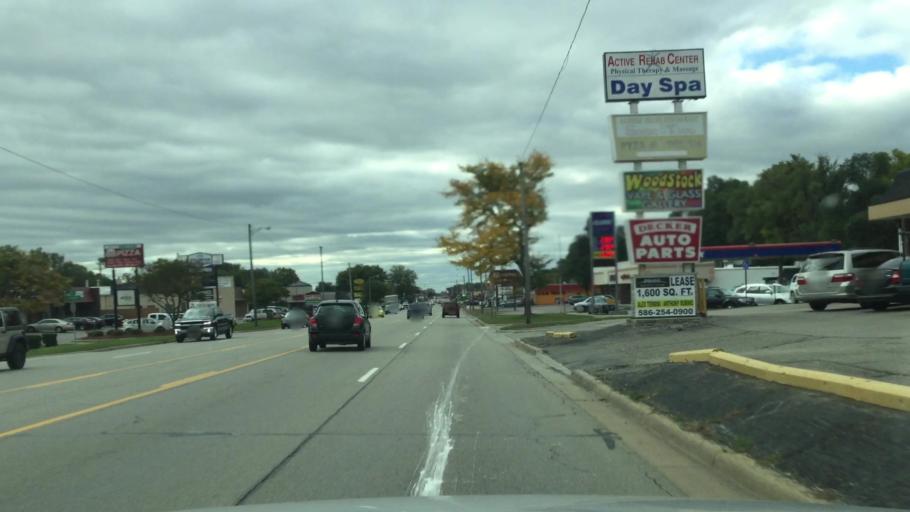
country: US
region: Michigan
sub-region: Macomb County
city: Utica
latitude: 42.6381
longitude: -83.0329
